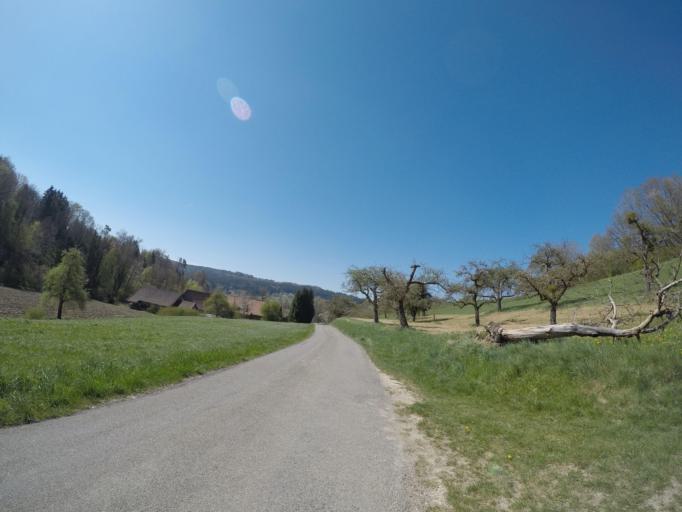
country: DE
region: Baden-Wuerttemberg
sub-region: Tuebingen Region
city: Oberteuringen
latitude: 47.7722
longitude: 9.4303
